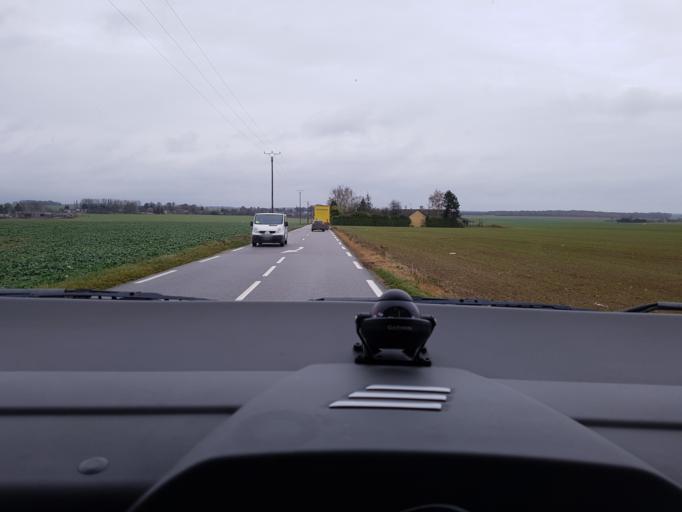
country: FR
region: Haute-Normandie
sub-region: Departement de l'Eure
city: Etrepagny
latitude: 49.3735
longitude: 1.5766
